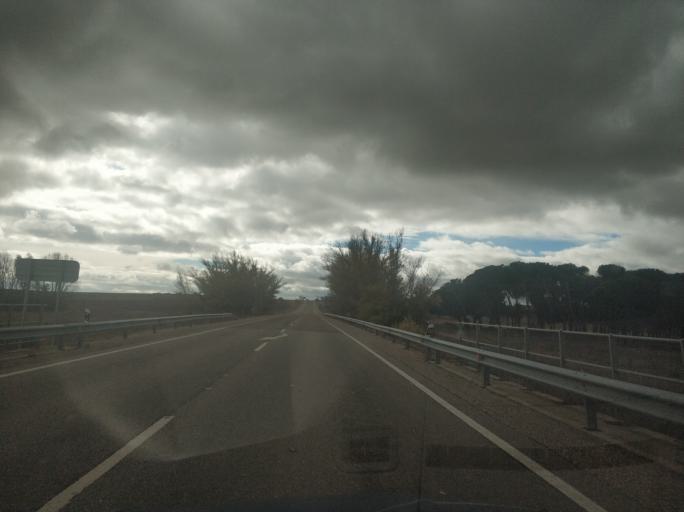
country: ES
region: Castille and Leon
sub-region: Provincia de Zamora
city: Castrillo de la Guarena
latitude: 41.2289
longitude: -5.3117
